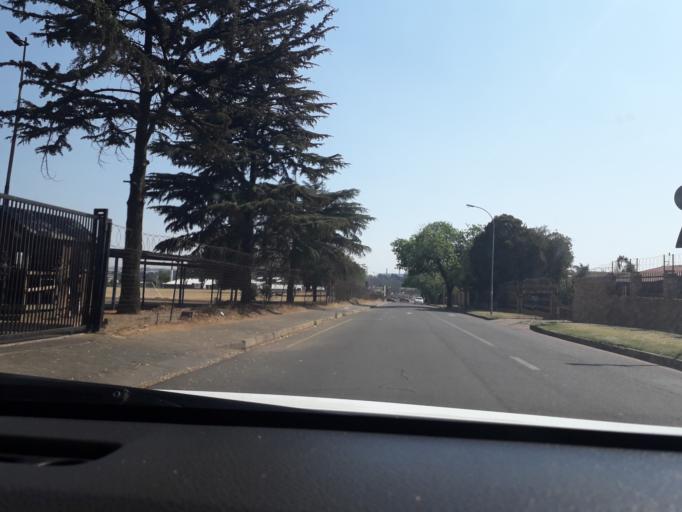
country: ZA
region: Gauteng
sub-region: City of Johannesburg Metropolitan Municipality
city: Modderfontein
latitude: -26.0974
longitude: 28.2251
